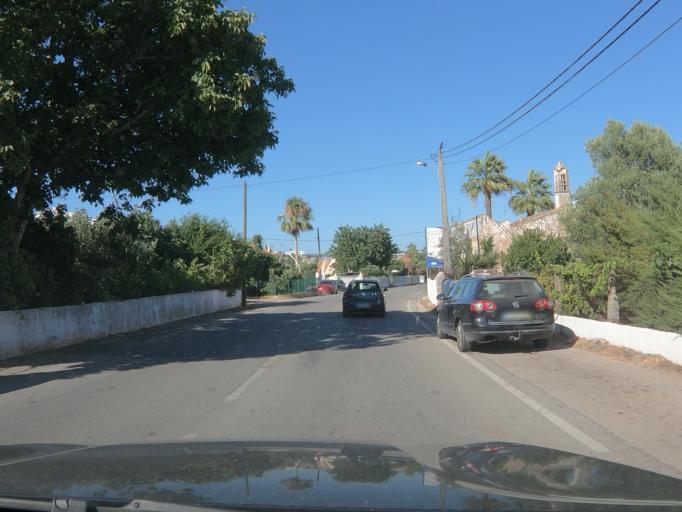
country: PT
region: Faro
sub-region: Loule
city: Almancil
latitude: 37.1021
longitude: -8.0587
